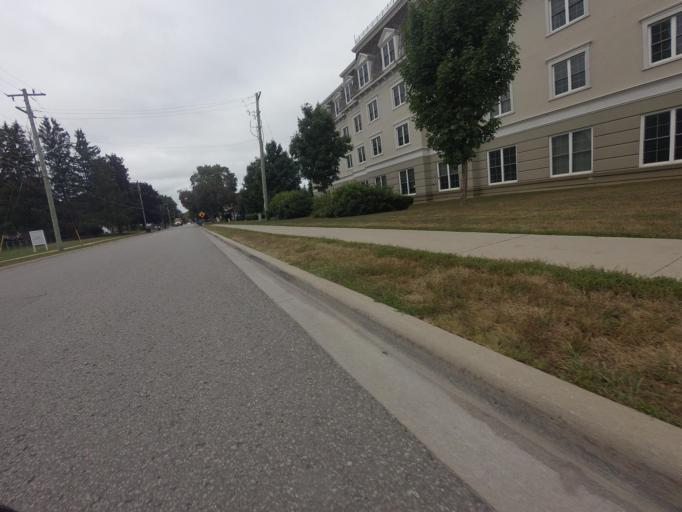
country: CA
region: Ontario
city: Omemee
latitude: 44.3459
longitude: -78.7450
